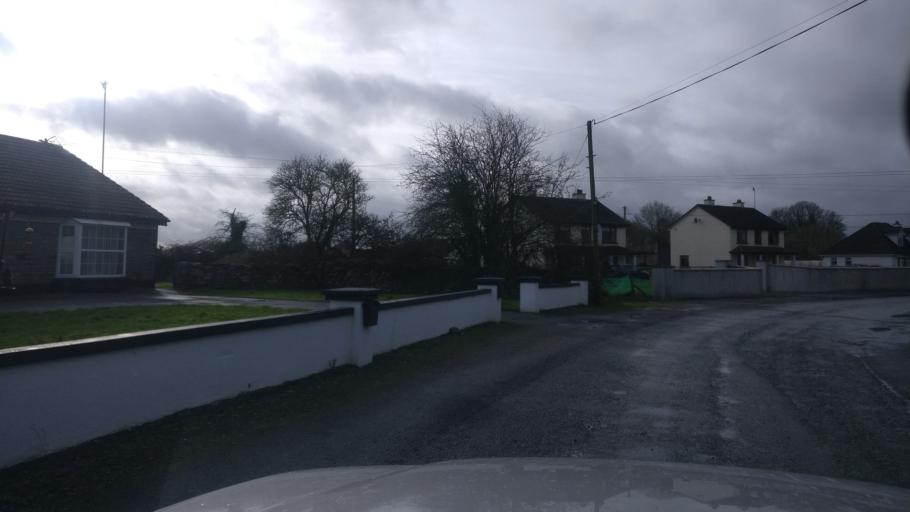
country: IE
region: Connaught
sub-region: County Galway
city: Athenry
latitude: 53.2633
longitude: -8.7938
